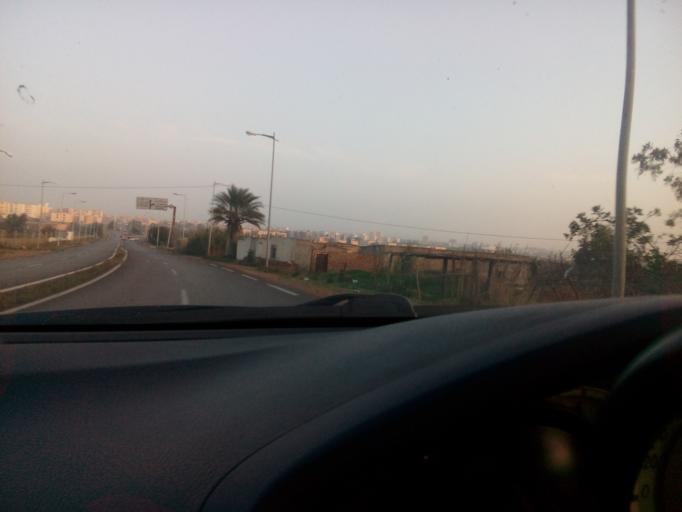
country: DZ
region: Oran
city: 'Ain el Turk
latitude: 35.7254
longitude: -0.7723
